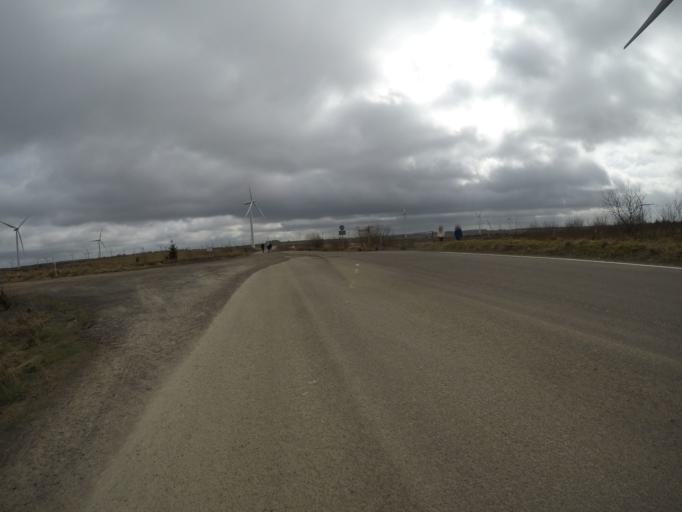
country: GB
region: Scotland
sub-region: East Renfrewshire
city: Newton Mearns
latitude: 55.7033
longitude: -4.3555
